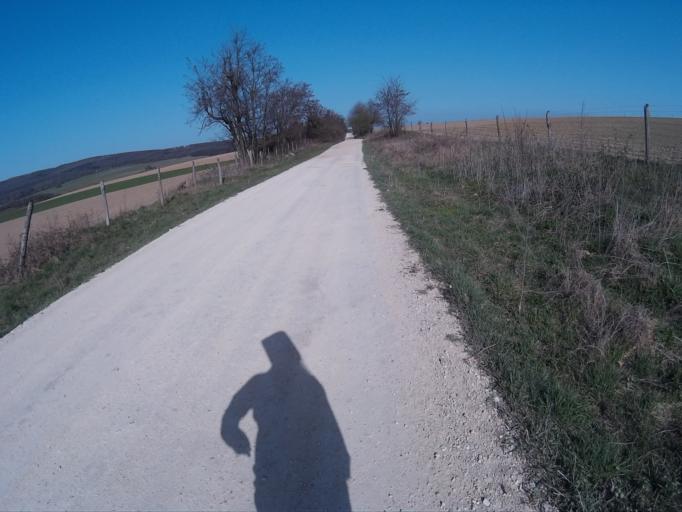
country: HU
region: Veszprem
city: Herend
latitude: 47.1943
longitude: 17.7963
